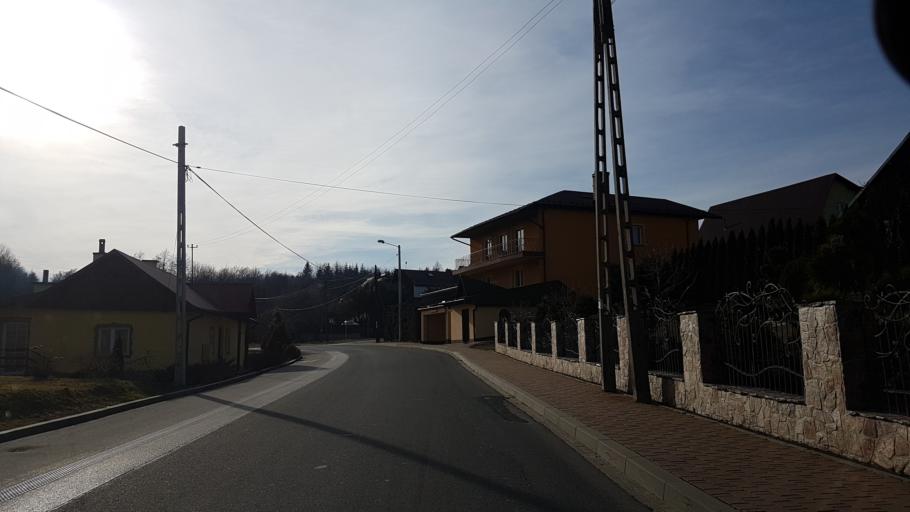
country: PL
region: Lesser Poland Voivodeship
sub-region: Powiat nowosadecki
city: Stary Sacz
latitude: 49.5427
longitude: 20.6358
